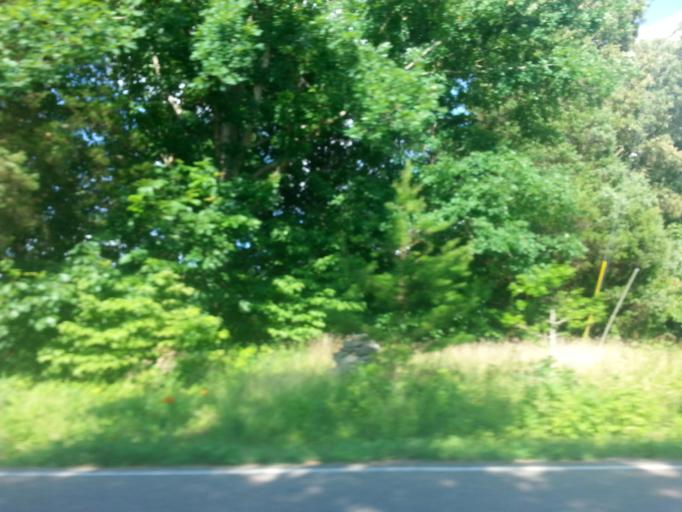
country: US
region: Tennessee
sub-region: Knox County
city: Knoxville
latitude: 36.0876
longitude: -83.8991
